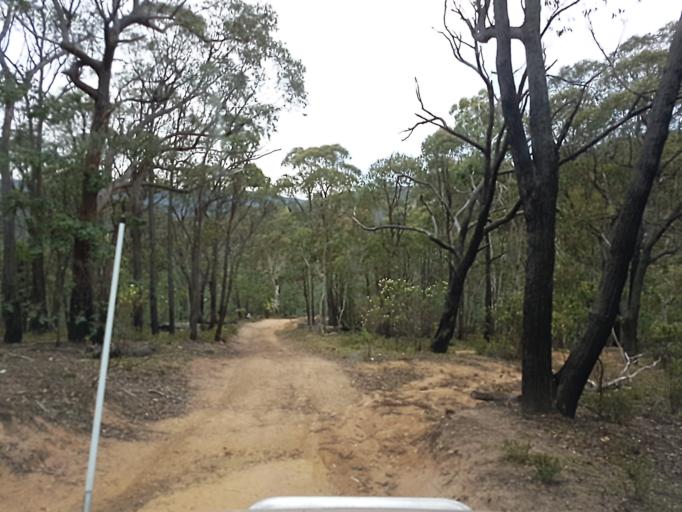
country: AU
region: New South Wales
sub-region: Snowy River
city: Jindabyne
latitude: -36.8694
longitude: 148.3291
